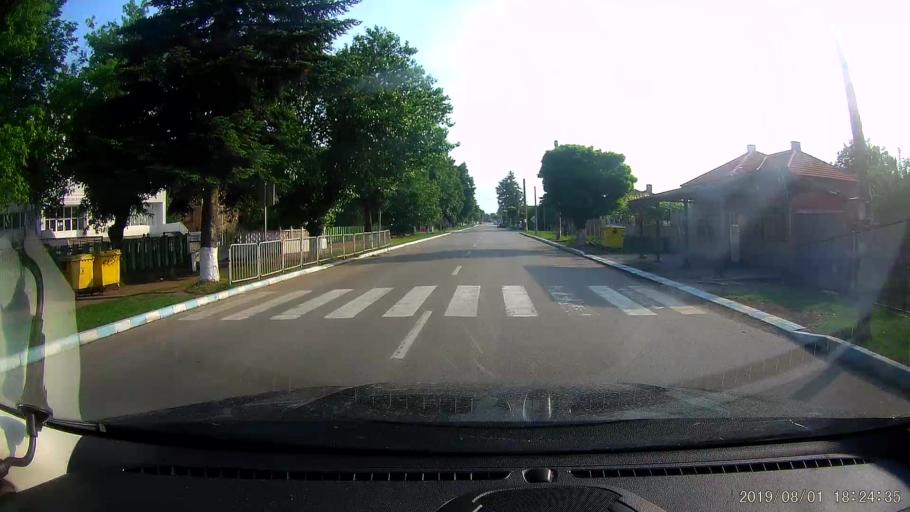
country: BG
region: Shumen
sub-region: Obshtina Venets
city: Venets
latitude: 43.6241
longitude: 27.0052
